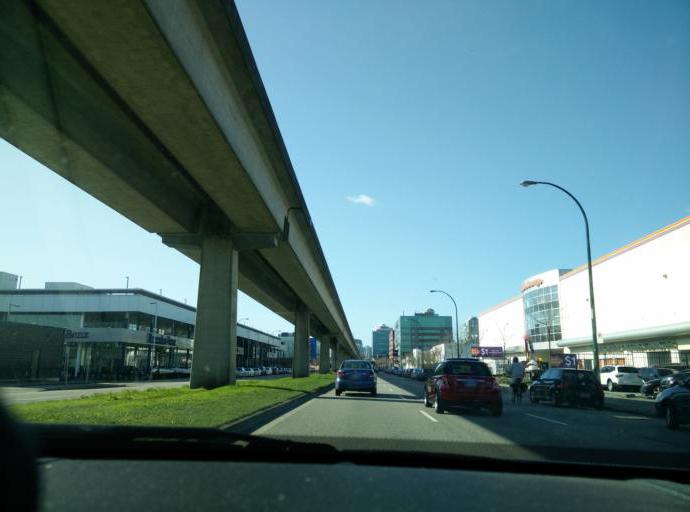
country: CA
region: British Columbia
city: Vancouver
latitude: 49.2712
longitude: -123.0900
